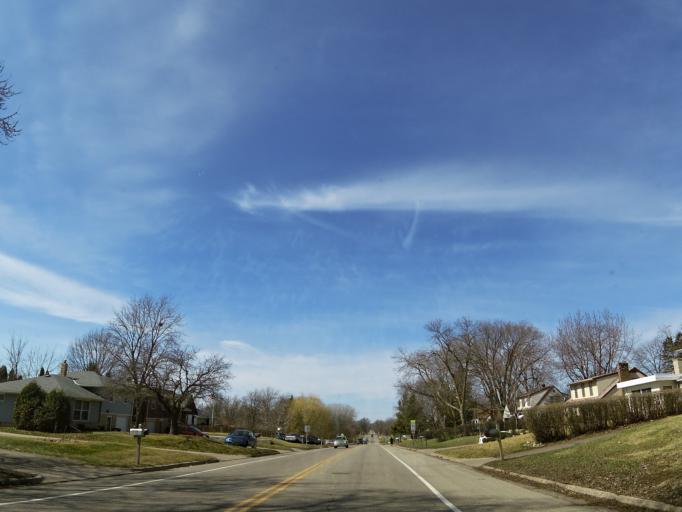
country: US
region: Minnesota
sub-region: Ramsey County
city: North Saint Paul
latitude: 44.9921
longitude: -93.0283
